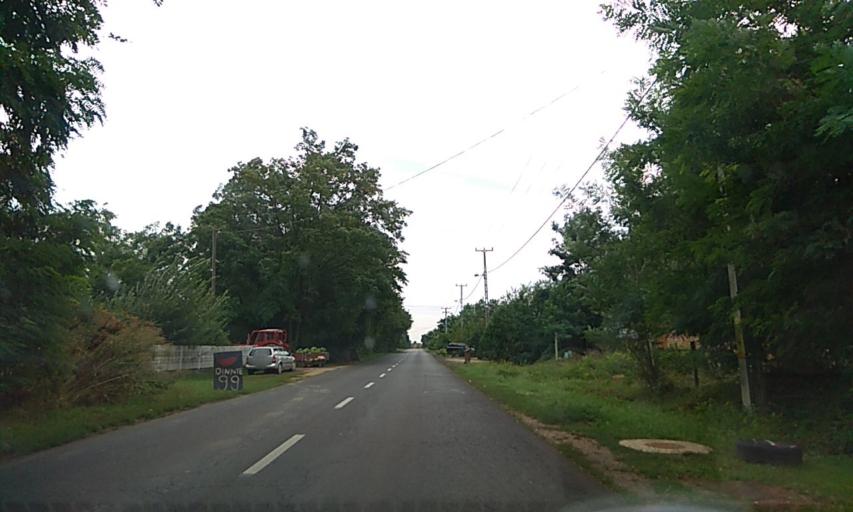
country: HU
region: Szabolcs-Szatmar-Bereg
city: Kotaj
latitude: 48.0219
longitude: 21.6820
